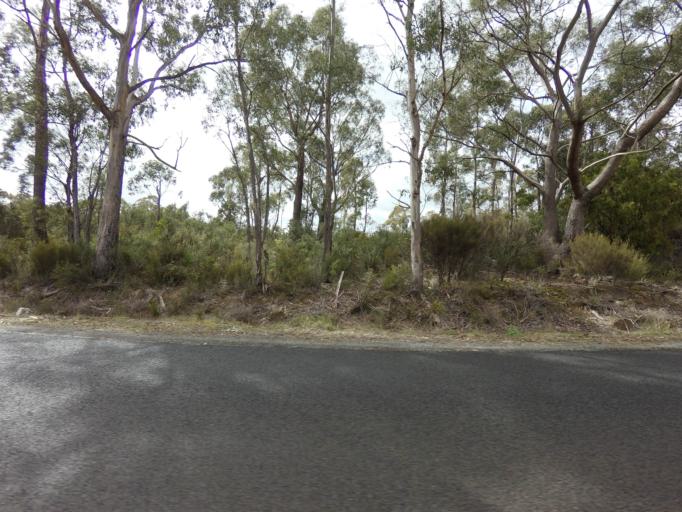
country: AU
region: Tasmania
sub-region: Huon Valley
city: Geeveston
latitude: -43.4443
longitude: 146.9040
